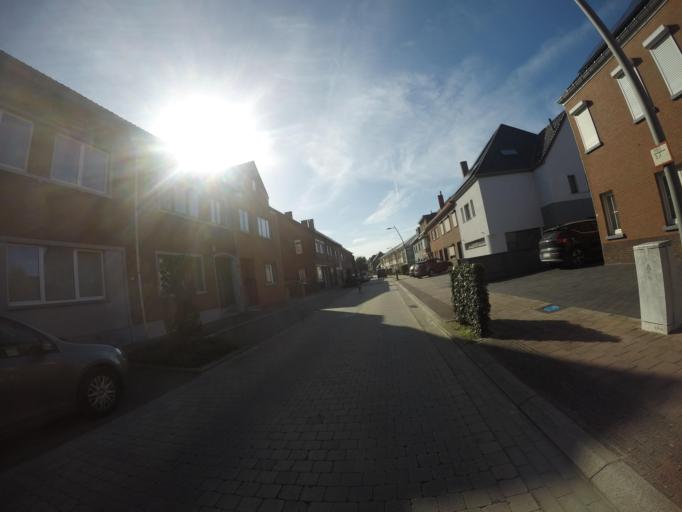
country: BE
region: Flanders
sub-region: Provincie Limburg
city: Diepenbeek
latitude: 50.9064
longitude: 5.4211
